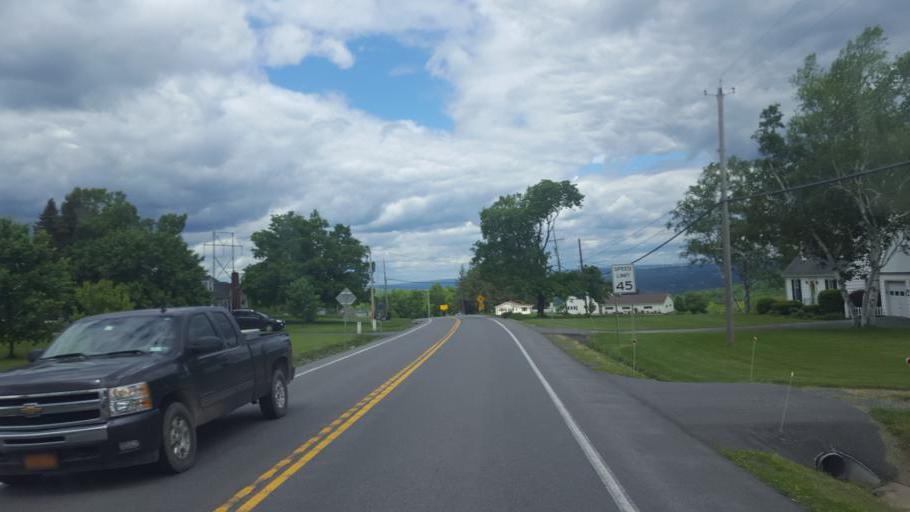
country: US
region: New York
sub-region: Herkimer County
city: Mohawk
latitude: 42.9805
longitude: -75.0096
